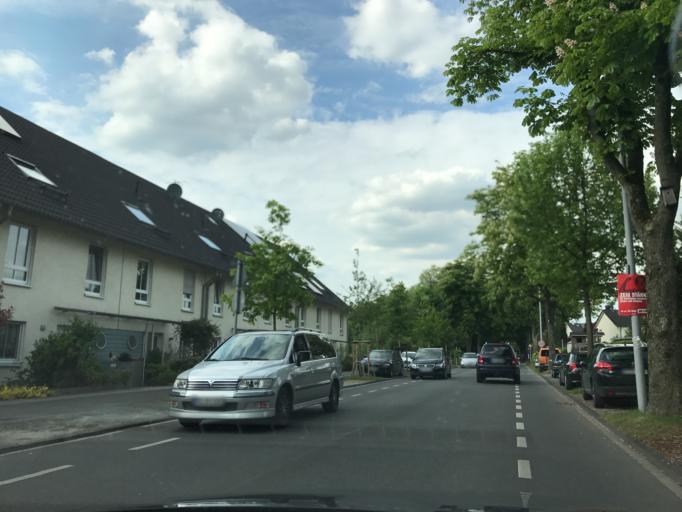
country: DE
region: North Rhine-Westphalia
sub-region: Regierungsbezirk Dusseldorf
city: Muelheim (Ruhr)
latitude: 51.4128
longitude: 6.9071
